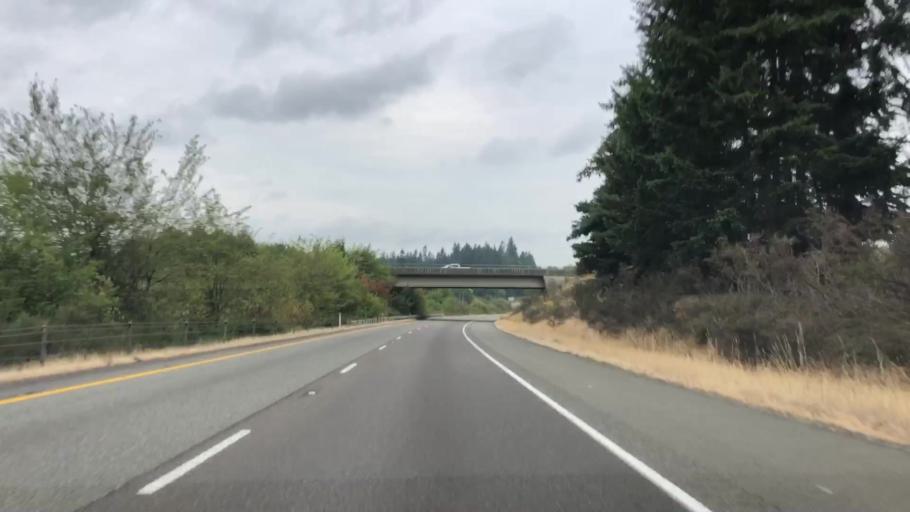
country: US
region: Washington
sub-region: Kitsap County
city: Bethel
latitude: 47.5002
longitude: -122.6447
